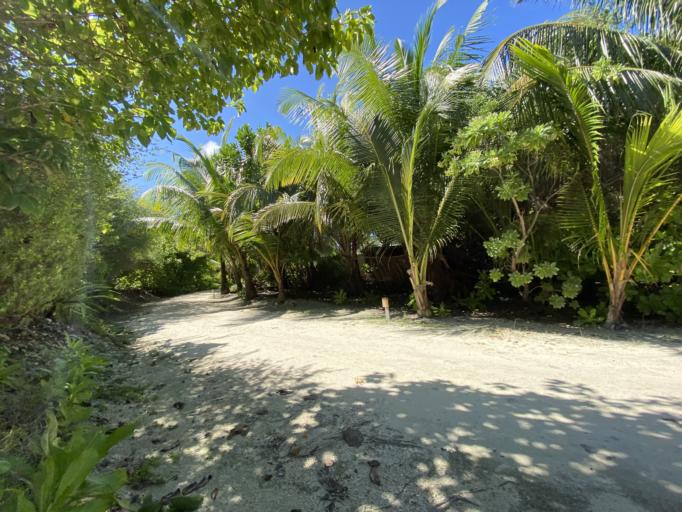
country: MV
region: Seenu
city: Meedhoo
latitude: -0.6399
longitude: 73.2233
